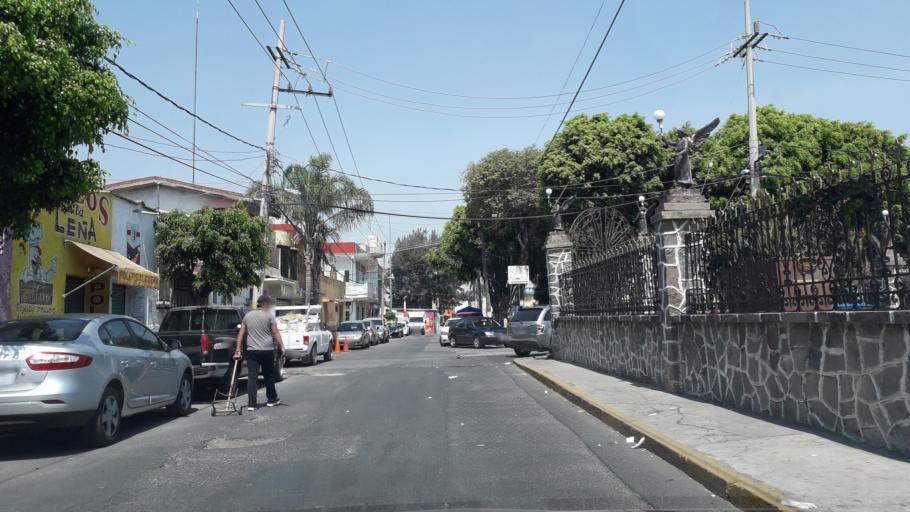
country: MX
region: Puebla
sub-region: Cuautlancingo
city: Sanctorum
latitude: 19.0904
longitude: -98.2152
